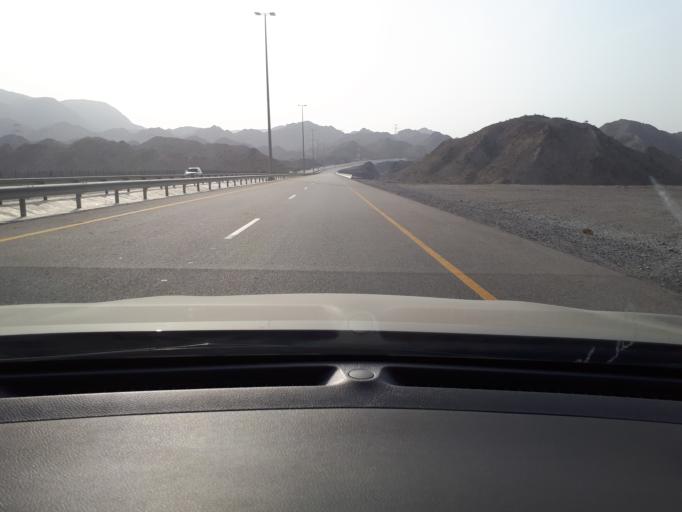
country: OM
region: Muhafazat Masqat
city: Muscat
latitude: 23.2102
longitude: 58.8024
